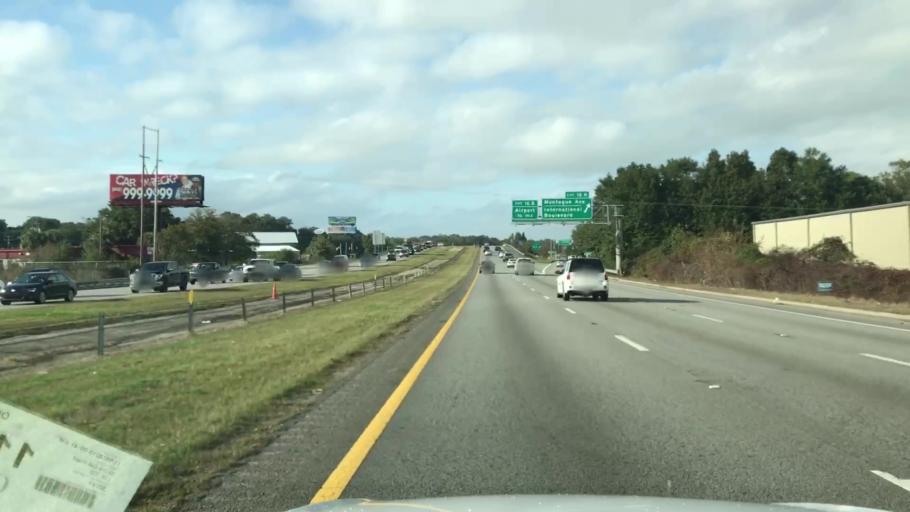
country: US
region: South Carolina
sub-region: Charleston County
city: North Charleston
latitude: 32.8593
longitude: -80.0238
